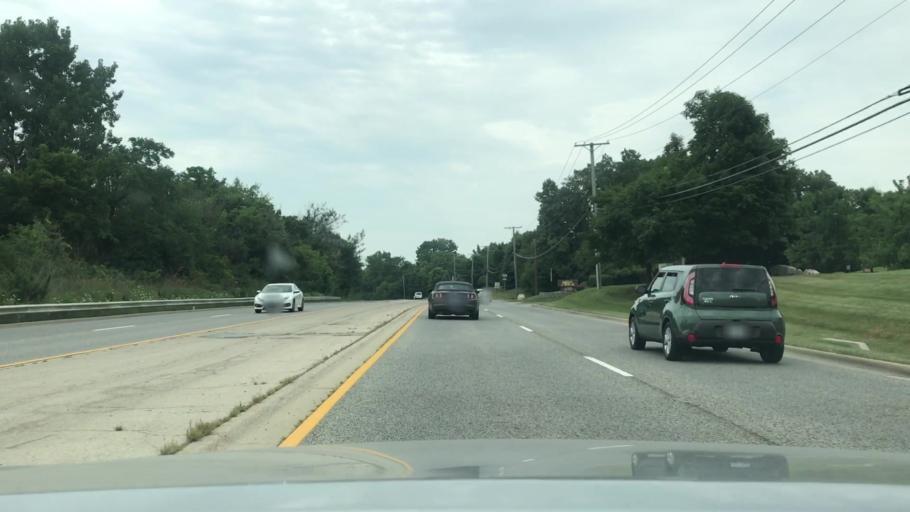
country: US
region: Illinois
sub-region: DuPage County
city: Woodridge
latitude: 41.7451
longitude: -88.0627
